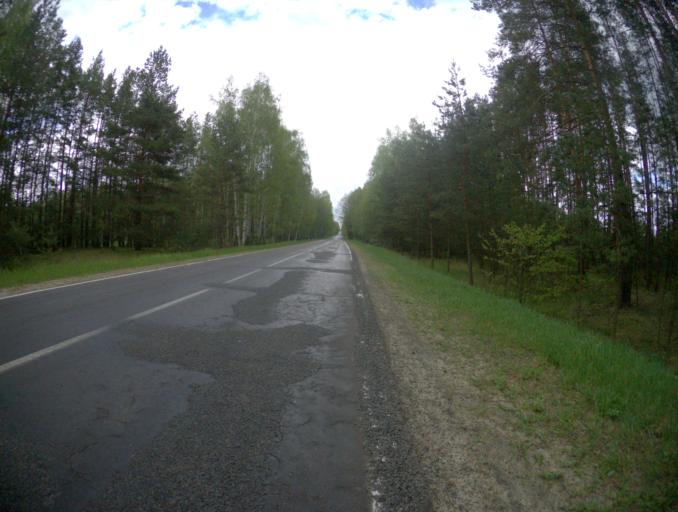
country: RU
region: Vladimir
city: Gusevskiy
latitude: 55.5759
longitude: 40.5133
